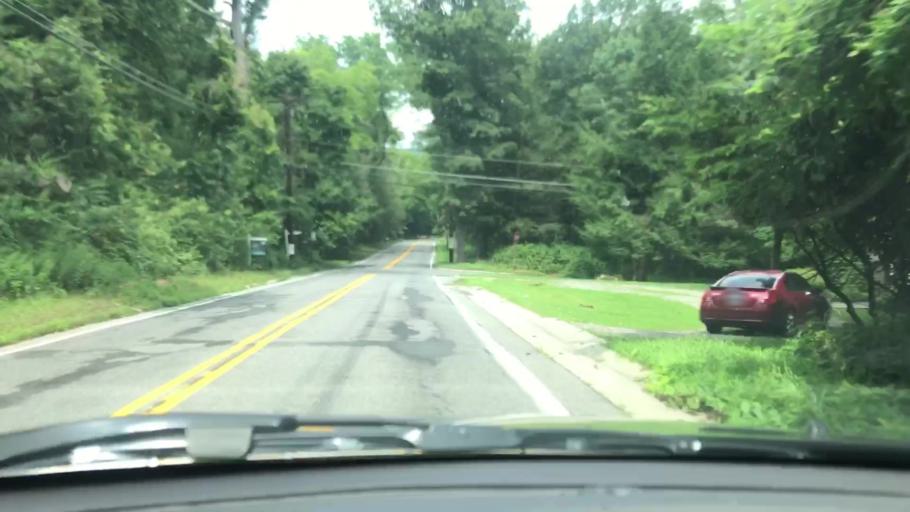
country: US
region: New York
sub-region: Westchester County
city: Bedford
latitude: 41.1874
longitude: -73.6172
